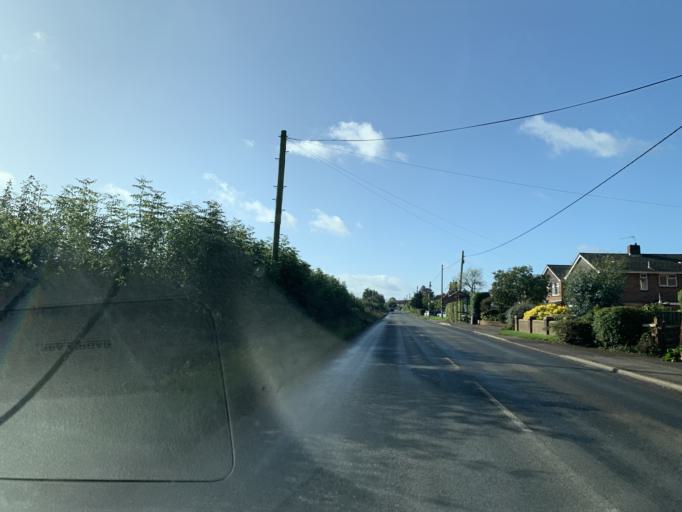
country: GB
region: England
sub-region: Wiltshire
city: Downton
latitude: 50.9862
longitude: -1.7172
